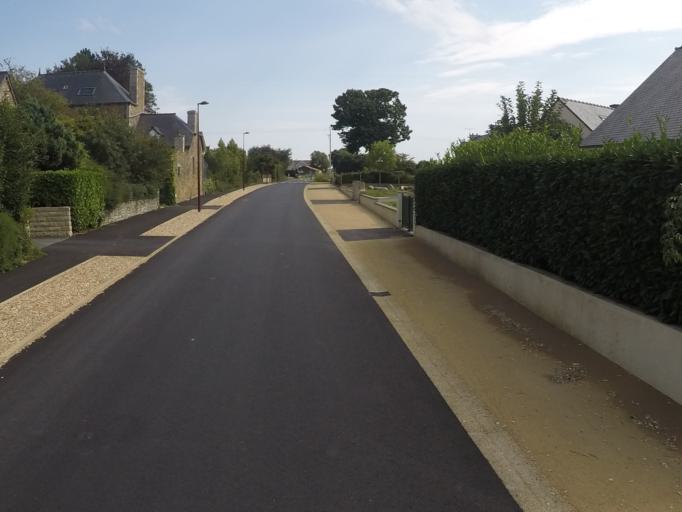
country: FR
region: Brittany
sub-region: Departement des Cotes-d'Armor
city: Goudelin
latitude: 48.6006
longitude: -3.0142
